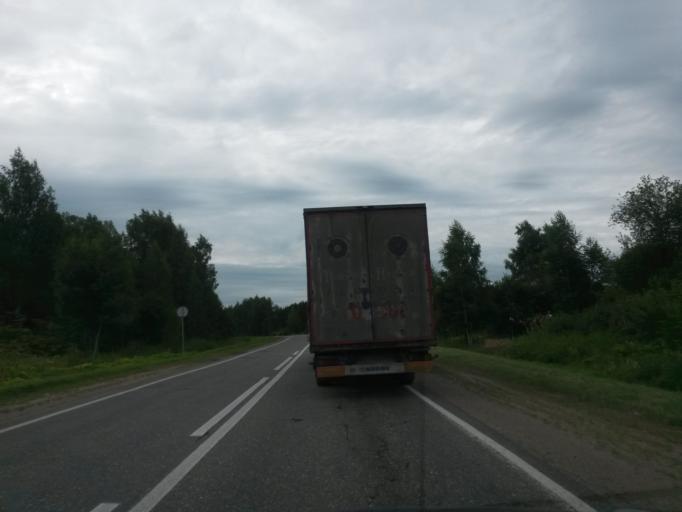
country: RU
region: Jaroslavl
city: Krasnyye Tkachi
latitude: 57.3671
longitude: 39.7370
